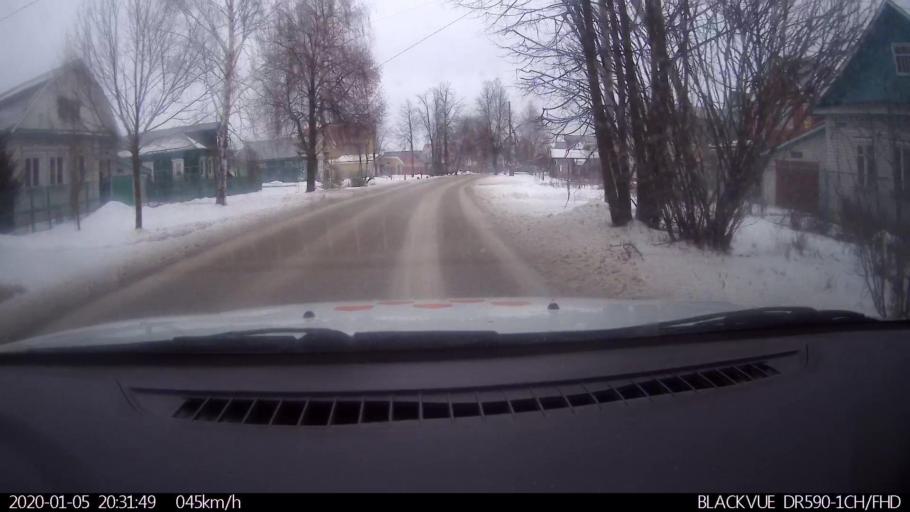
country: RU
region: Nizjnij Novgorod
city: Lukino
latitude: 56.4087
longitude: 43.7285
